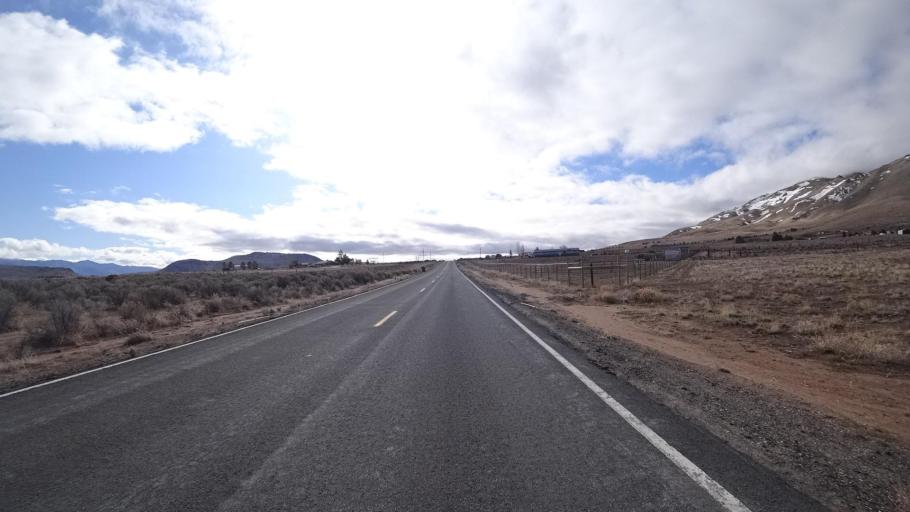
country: US
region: Nevada
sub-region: Washoe County
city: Cold Springs
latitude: 39.8932
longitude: -119.9788
